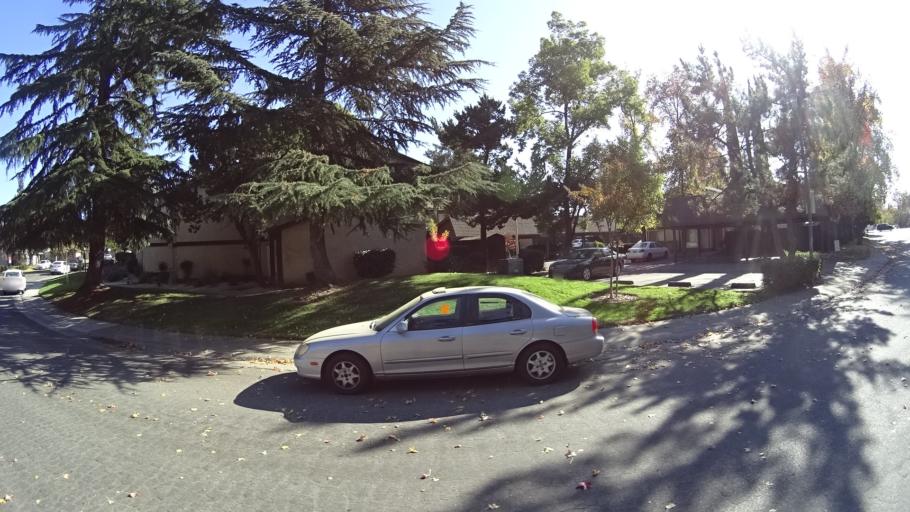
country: US
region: California
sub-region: Sacramento County
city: Antelope
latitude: 38.6792
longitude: -121.3164
